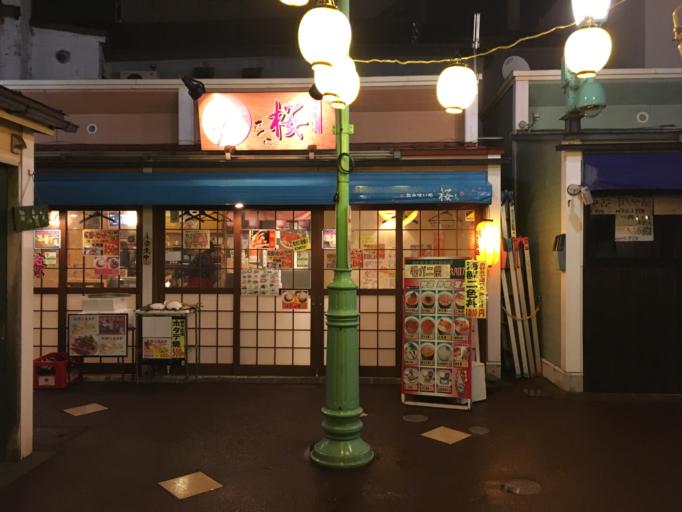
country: JP
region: Hokkaido
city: Hakodate
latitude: 41.7724
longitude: 140.7302
